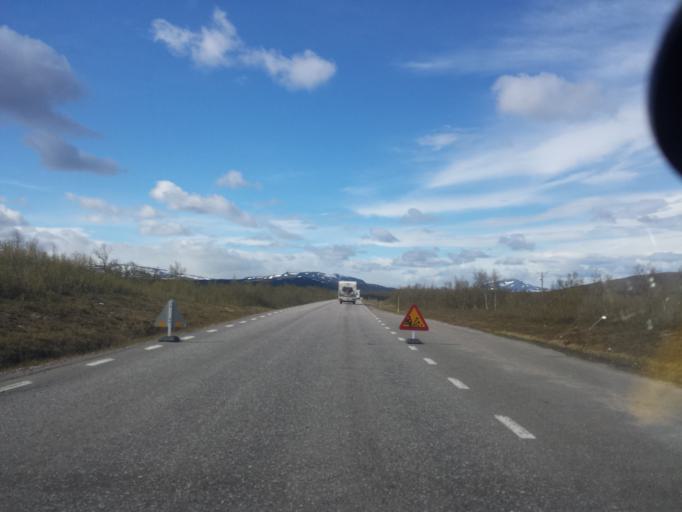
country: SE
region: Norrbotten
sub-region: Kiruna Kommun
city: Kiruna
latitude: 68.0079
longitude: 19.8477
